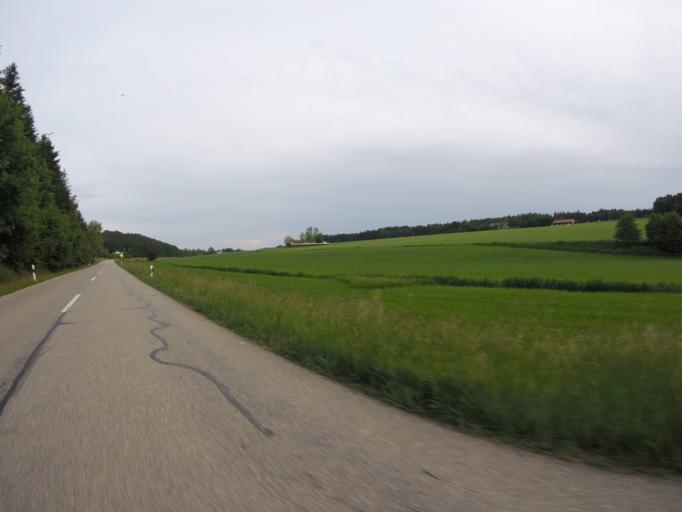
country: DE
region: Bavaria
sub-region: Upper Bavaria
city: Schweitenkirchen
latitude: 48.4816
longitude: 11.6093
